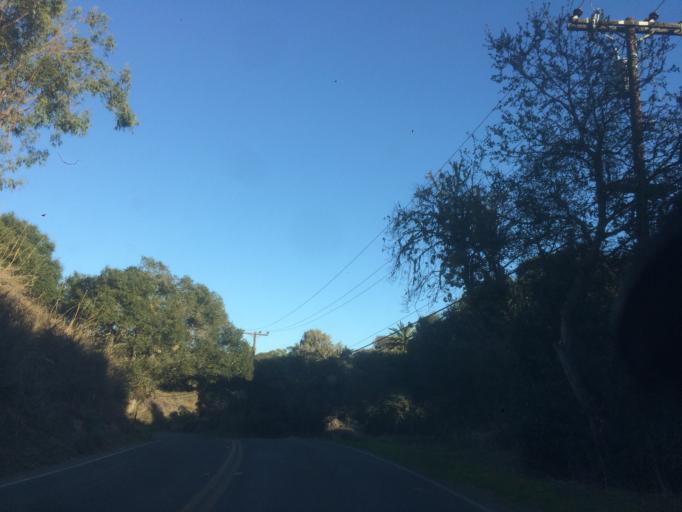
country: US
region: California
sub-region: Santa Barbara County
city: Santa Barbara
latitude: 34.4056
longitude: -119.7492
